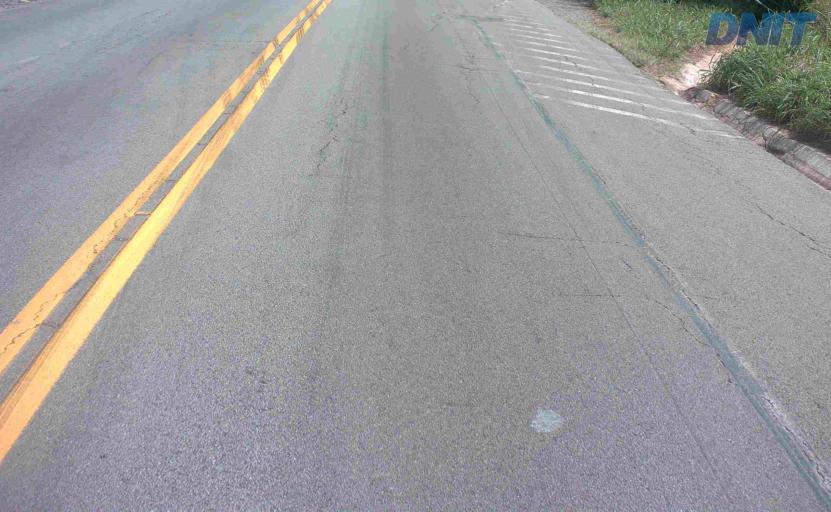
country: BR
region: Minas Gerais
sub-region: Santa Luzia
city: Santa Luzia
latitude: -19.8118
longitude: -43.7965
